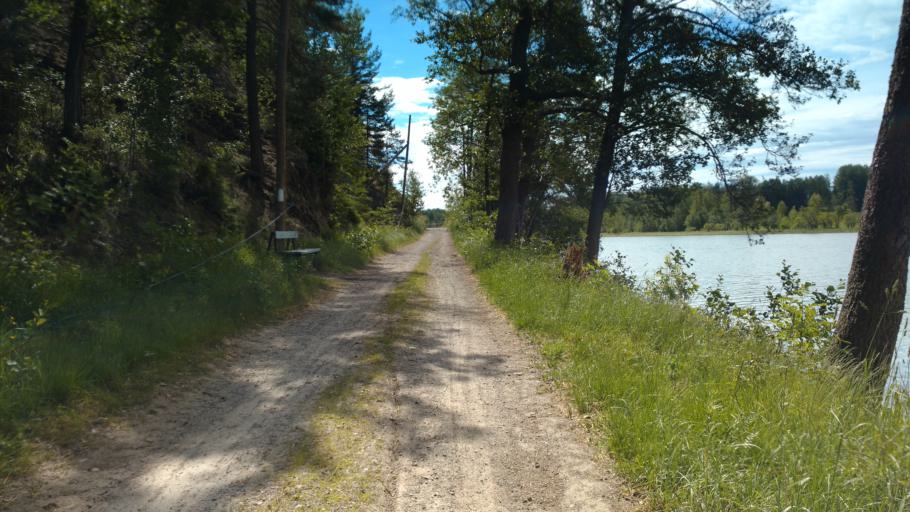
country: FI
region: Uusimaa
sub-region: Raaseporin
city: Pohja
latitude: 60.1128
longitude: 23.5441
